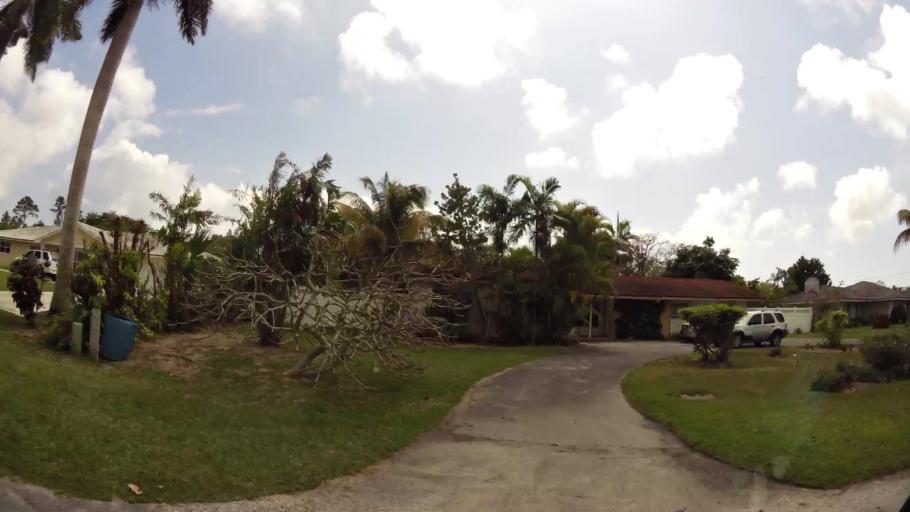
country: BS
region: Freeport
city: Freeport
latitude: 26.5152
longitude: -78.7098
